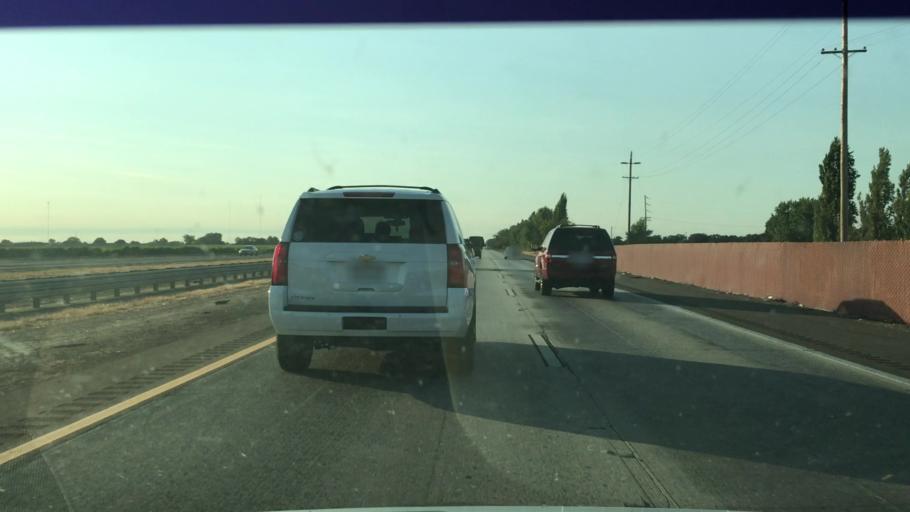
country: US
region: California
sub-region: San Joaquin County
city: Thornton
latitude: 38.1950
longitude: -121.4086
